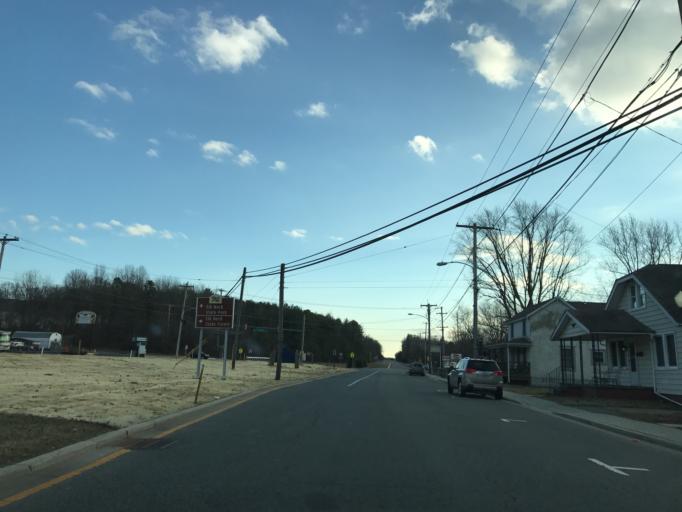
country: US
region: Maryland
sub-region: Cecil County
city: North East
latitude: 39.5933
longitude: -75.9415
